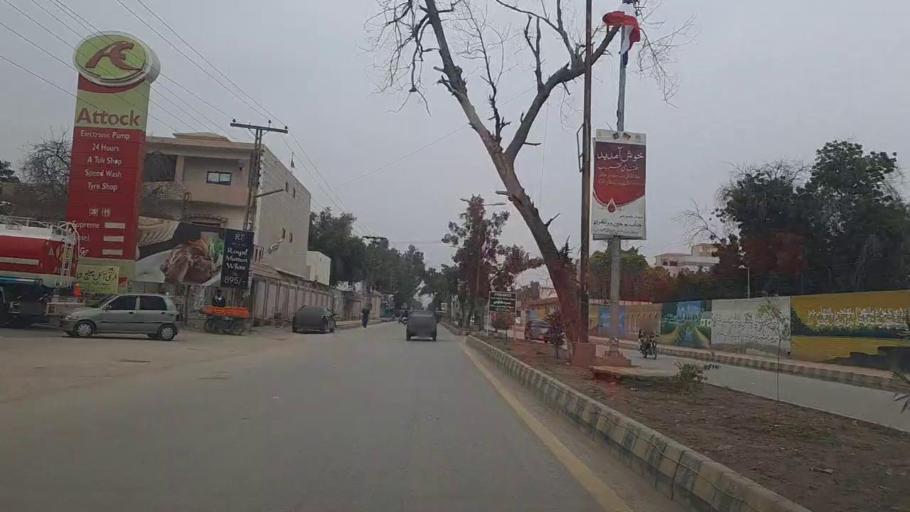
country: PK
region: Sindh
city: Nawabshah
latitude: 26.2439
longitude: 68.4016
